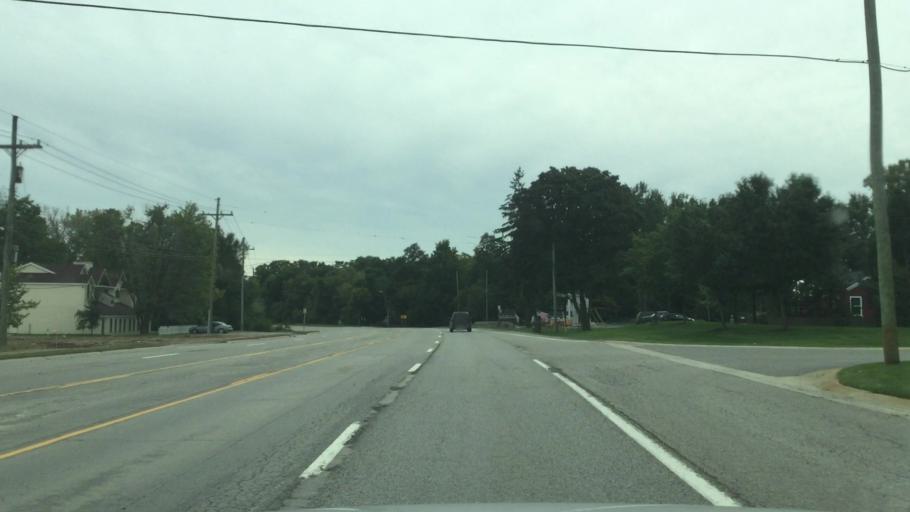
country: US
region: Michigan
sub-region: Oakland County
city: Clarkston
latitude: 42.7536
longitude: -83.4795
